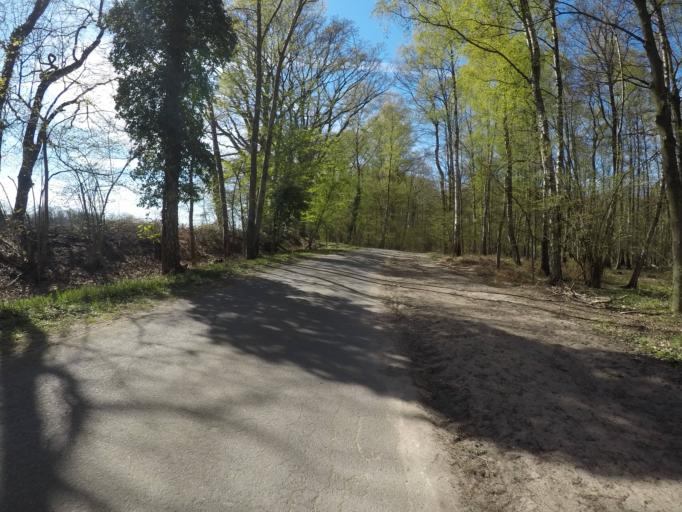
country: DE
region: Hamburg
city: Wohldorf-Ohlstedt
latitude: 53.7143
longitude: 10.1444
